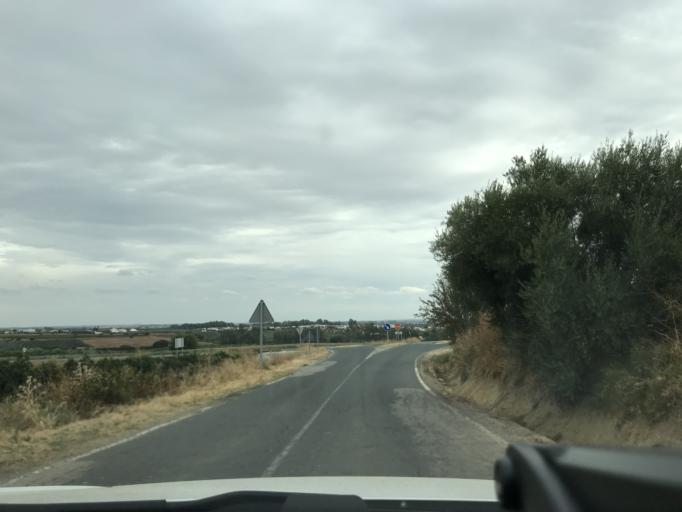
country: ES
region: Andalusia
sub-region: Provincia de Sevilla
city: Villanueva del Rio y Minas
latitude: 37.6373
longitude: -5.7011
